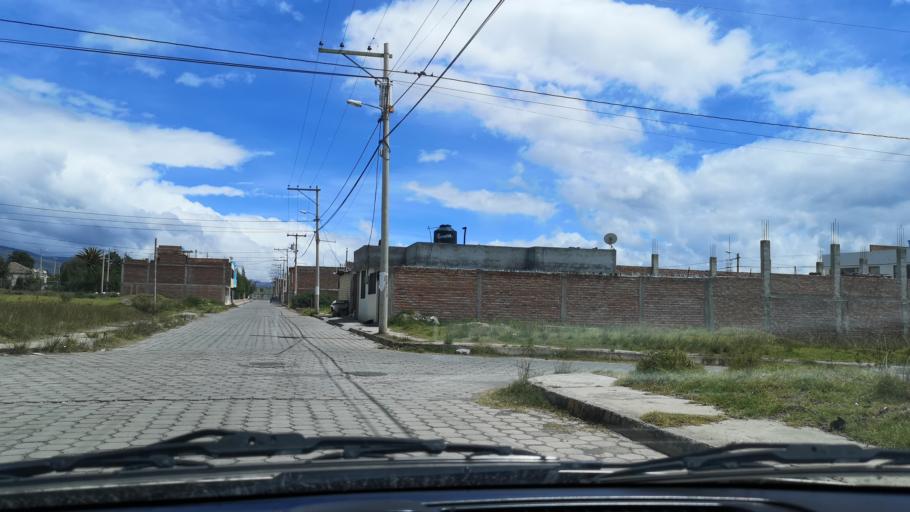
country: EC
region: Chimborazo
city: Riobamba
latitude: -1.6412
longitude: -78.6842
